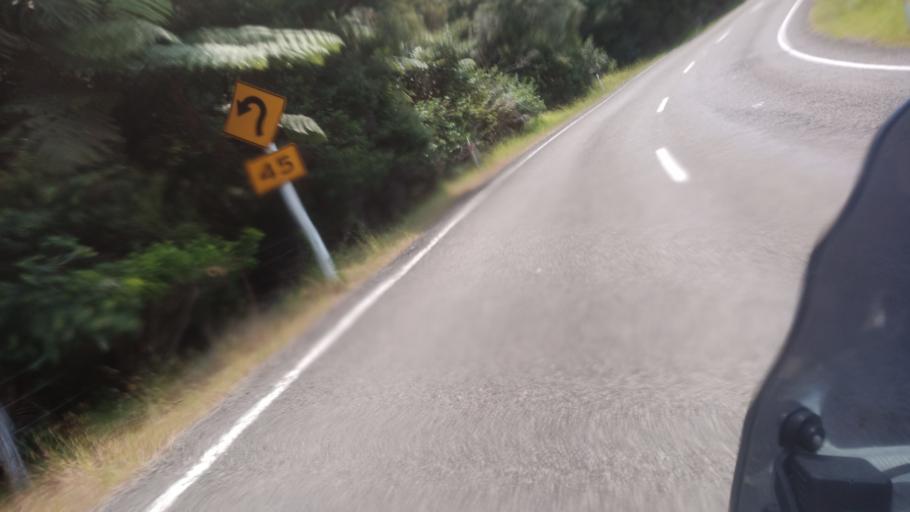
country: NZ
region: Bay of Plenty
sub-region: Opotiki District
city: Opotiki
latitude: -37.5754
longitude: 178.1058
